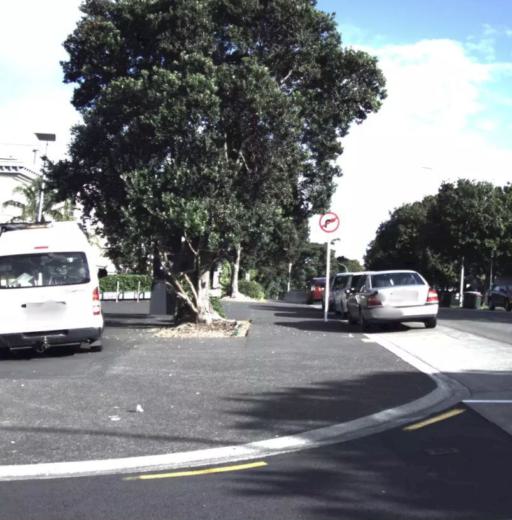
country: NZ
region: Auckland
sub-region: Auckland
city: Auckland
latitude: -36.8741
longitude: 174.7467
